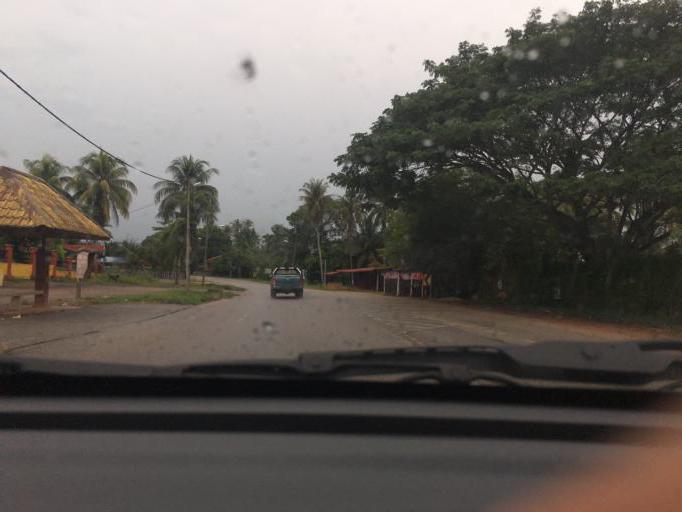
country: MY
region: Kedah
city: Bedong
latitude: 5.6920
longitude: 100.6317
